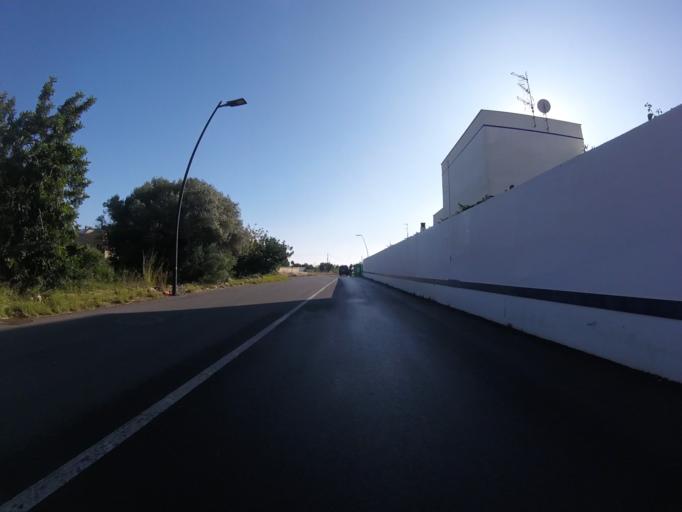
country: ES
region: Valencia
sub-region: Provincia de Castello
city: Peniscola
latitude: 40.3822
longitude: 0.3837
